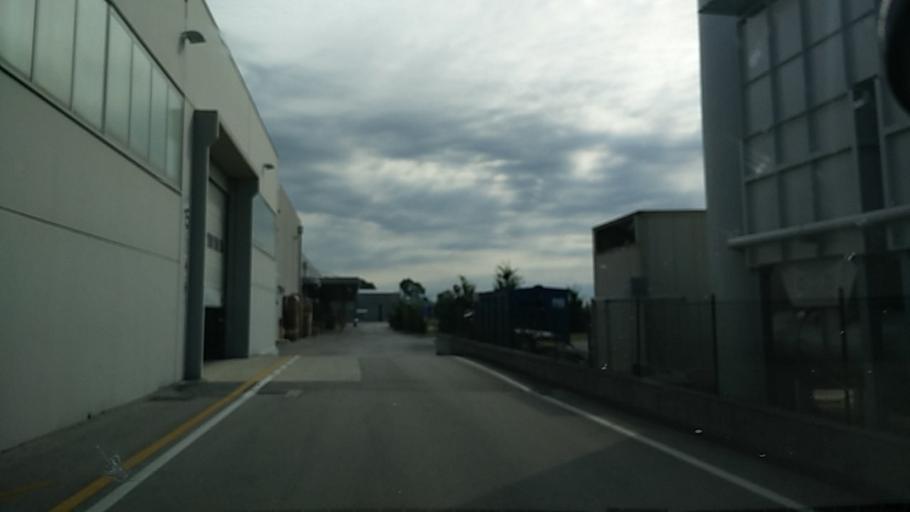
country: IT
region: Veneto
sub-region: Provincia di Treviso
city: Portobuffole
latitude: 45.8533
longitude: 12.5088
